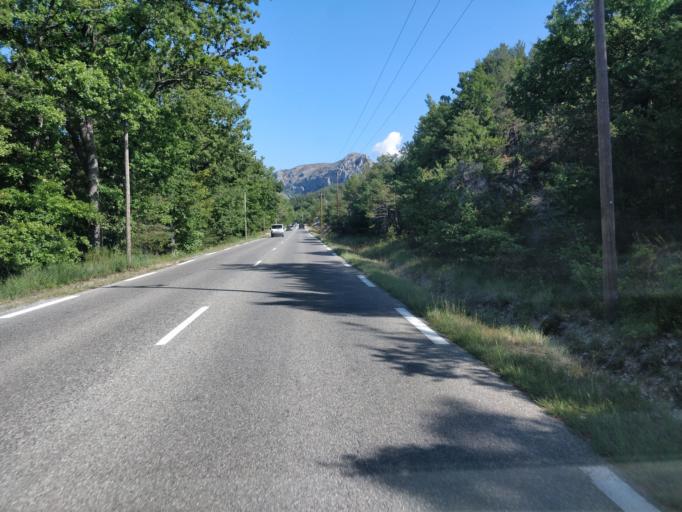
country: FR
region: Provence-Alpes-Cote d'Azur
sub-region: Departement des Alpes-de-Haute-Provence
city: Riez
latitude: 43.8153
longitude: 6.2265
